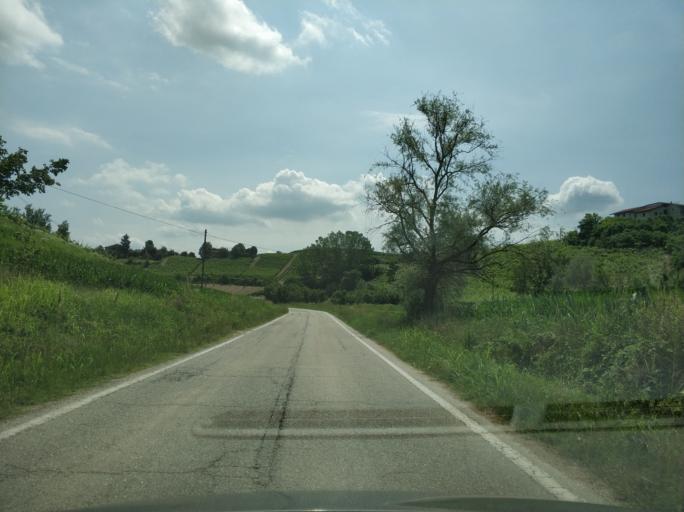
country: IT
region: Piedmont
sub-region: Provincia di Cuneo
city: Santo Stefano Roero
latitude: 44.7846
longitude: 7.9620
